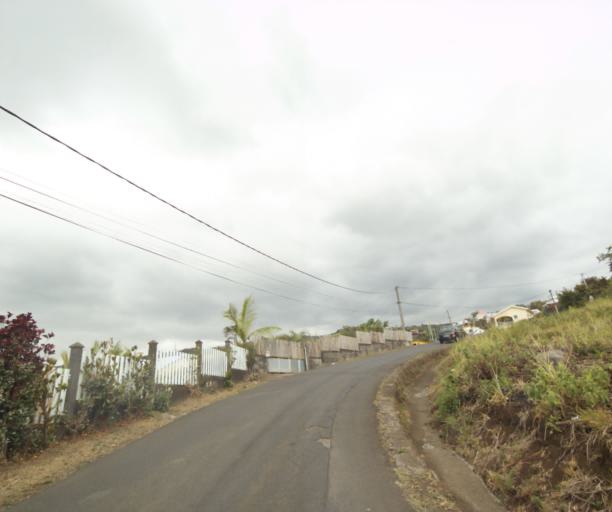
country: RE
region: Reunion
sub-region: Reunion
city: Saint-Paul
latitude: -21.0263
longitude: 55.3073
